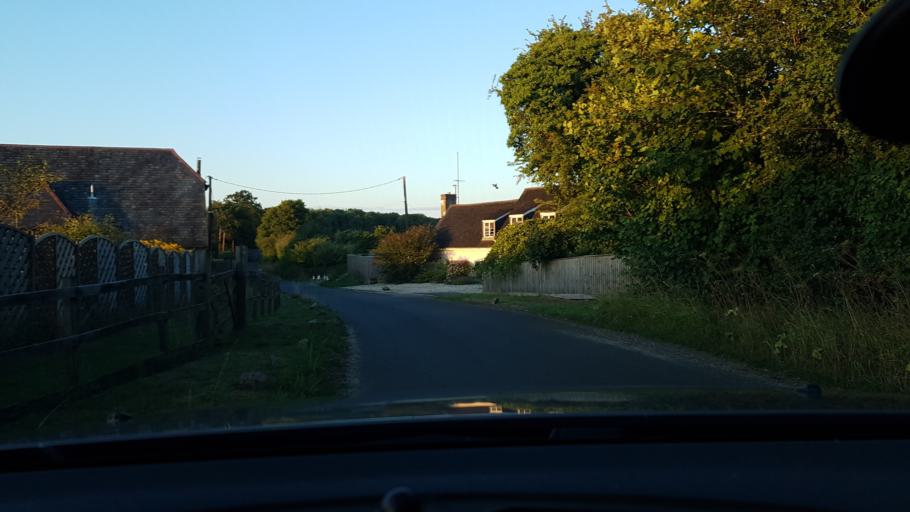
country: GB
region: England
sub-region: West Berkshire
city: Hungerford
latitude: 51.3950
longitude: -1.5218
